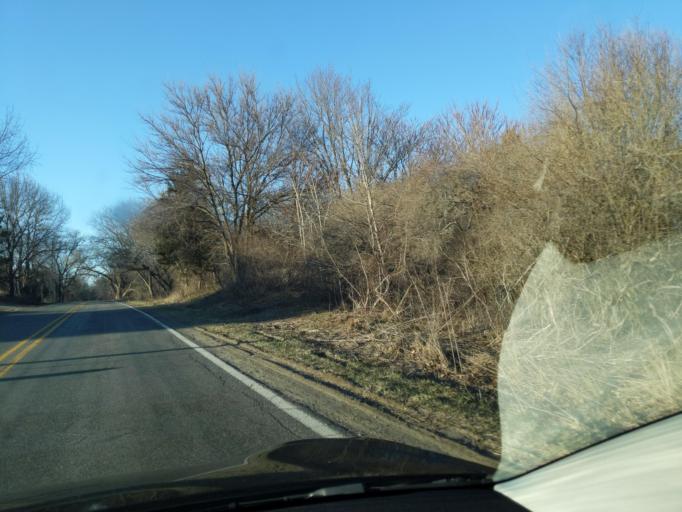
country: US
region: Michigan
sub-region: Washtenaw County
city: Chelsea
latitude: 42.4191
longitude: -84.0530
